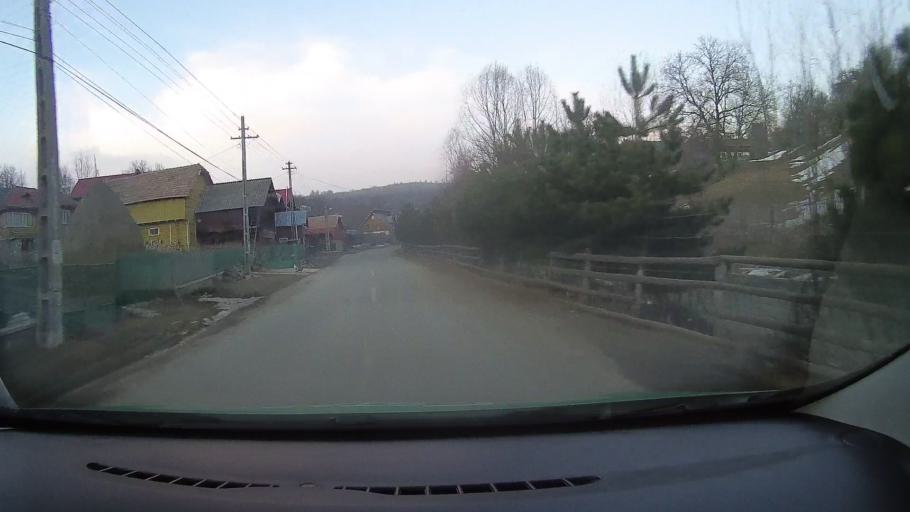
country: RO
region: Prahova
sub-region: Comuna Secaria
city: Secaria
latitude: 45.2742
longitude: 25.6864
